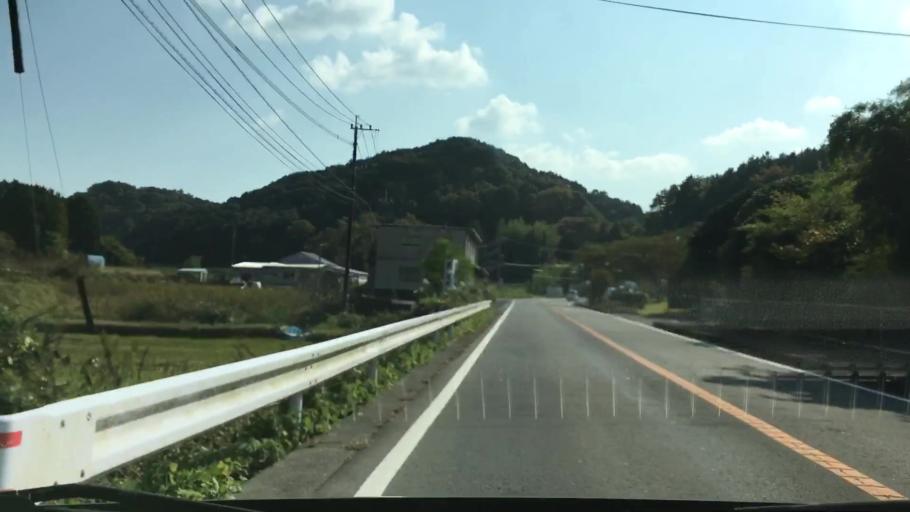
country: JP
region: Nagasaki
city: Togitsu
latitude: 32.9770
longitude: 129.7813
